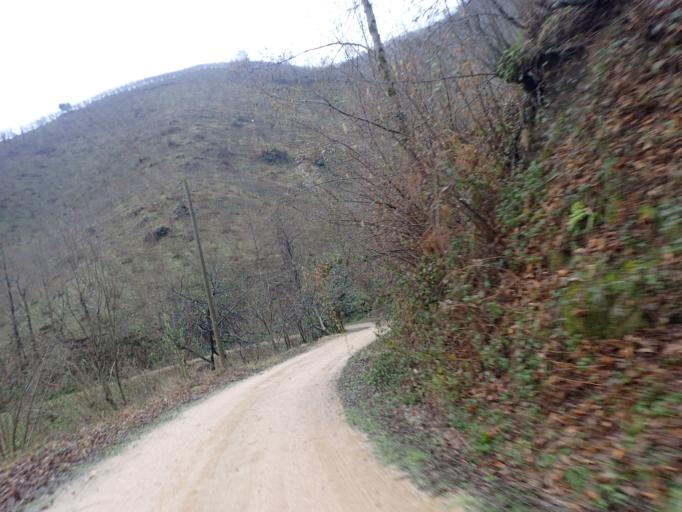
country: TR
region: Ordu
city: Camas
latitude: 40.9084
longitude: 37.5691
